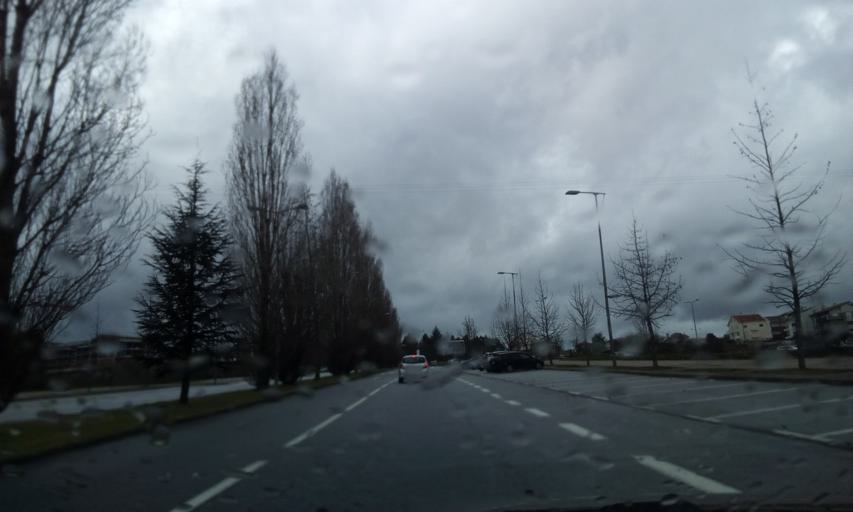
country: PT
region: Viseu
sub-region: Viseu
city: Abraveses
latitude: 40.6727
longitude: -7.9222
